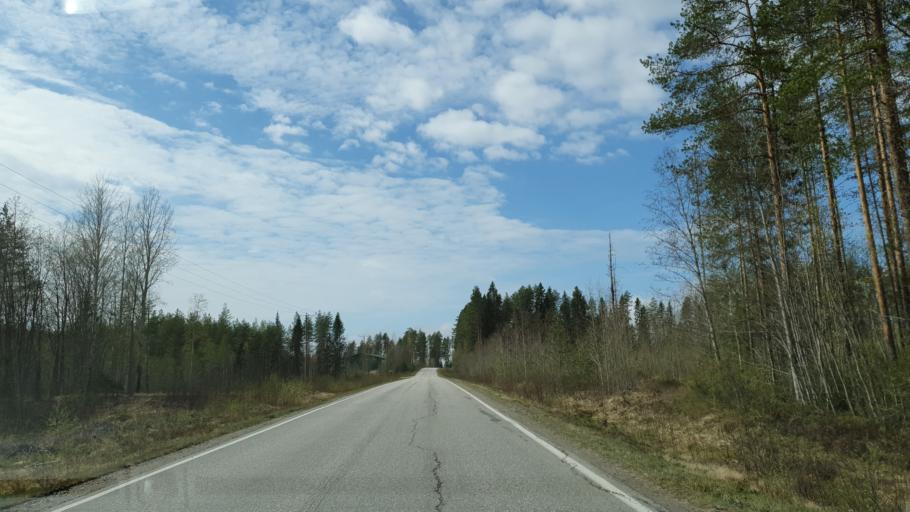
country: FI
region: Kainuu
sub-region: Kehys-Kainuu
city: Kuhmo
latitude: 64.1214
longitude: 29.6747
